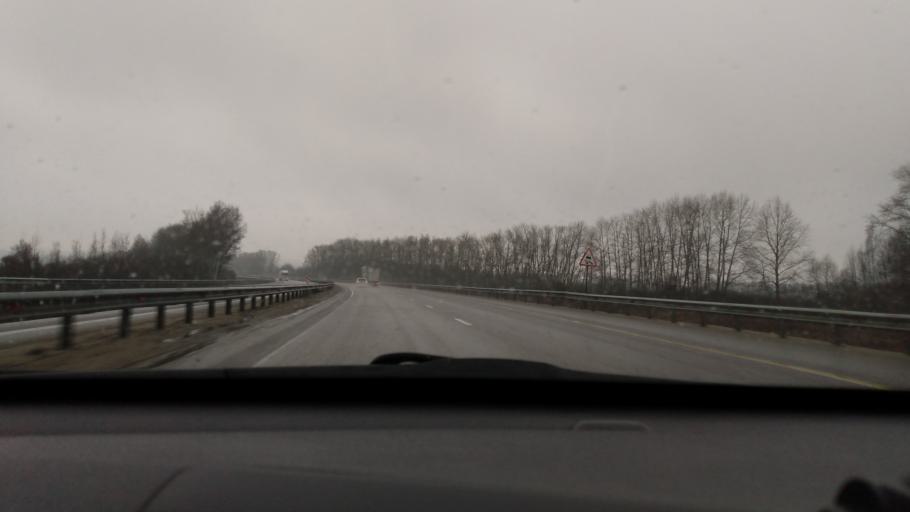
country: RU
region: Tula
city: Shvartsevskiy
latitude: 54.1317
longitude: 38.0577
